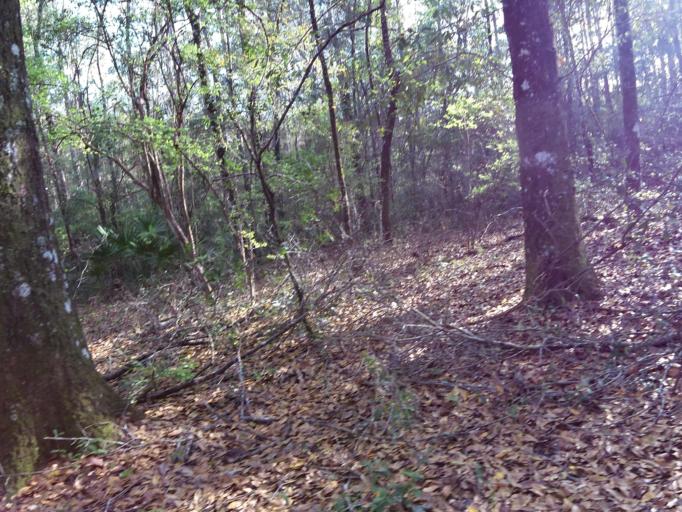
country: US
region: Florida
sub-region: Clay County
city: Middleburg
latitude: 30.1520
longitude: -81.9567
